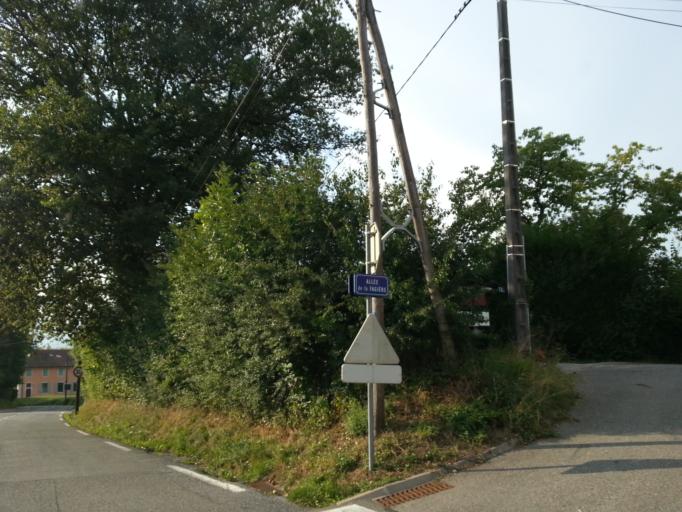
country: FR
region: Rhone-Alpes
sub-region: Departement de la Haute-Savoie
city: Annecy-le-Vieux
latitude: 45.9202
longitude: 6.1736
